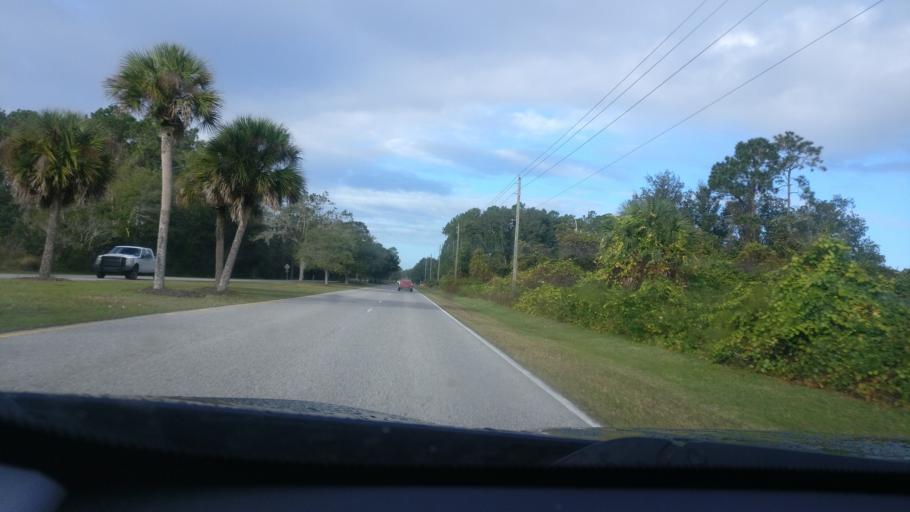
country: US
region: Florida
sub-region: Flagler County
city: Bunnell
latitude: 29.5218
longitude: -81.2485
